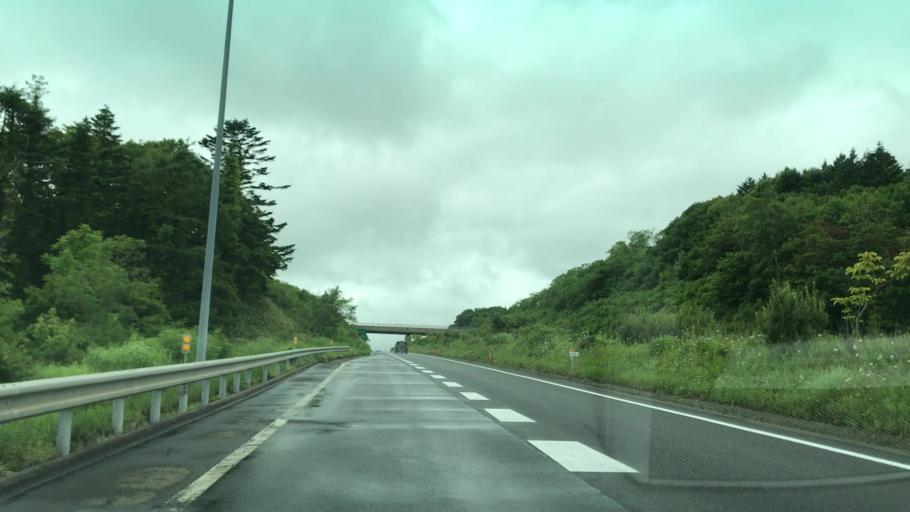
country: JP
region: Hokkaido
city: Muroran
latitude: 42.3849
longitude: 140.9863
